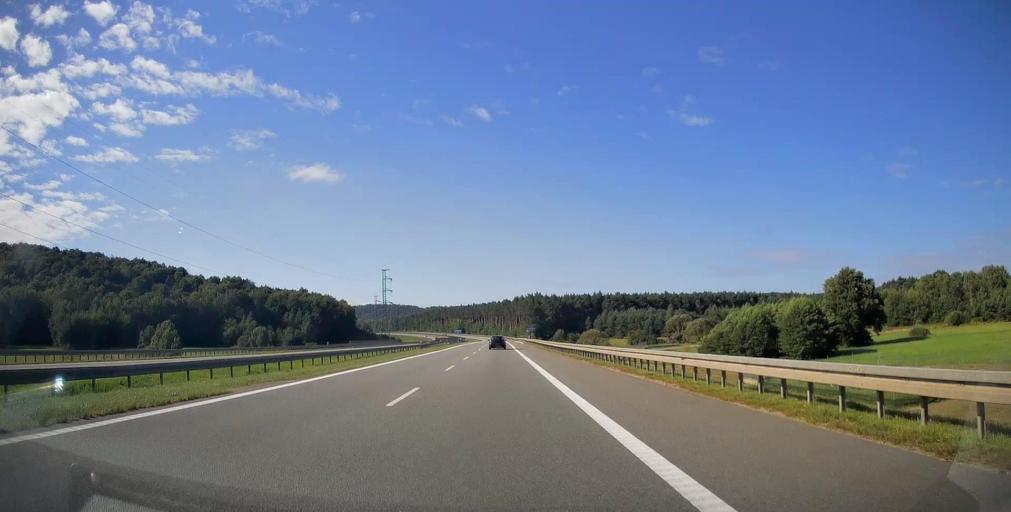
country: PL
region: Swietokrzyskie
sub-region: Powiat kielecki
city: Checiny
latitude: 50.8346
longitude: 20.4728
